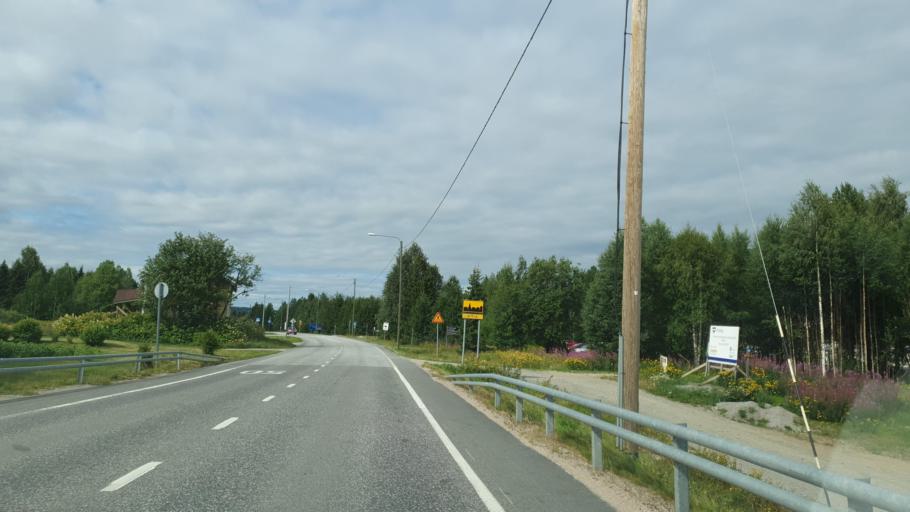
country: FI
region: Lapland
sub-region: Tunturi-Lappi
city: Kittilae
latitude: 67.6470
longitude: 24.9286
